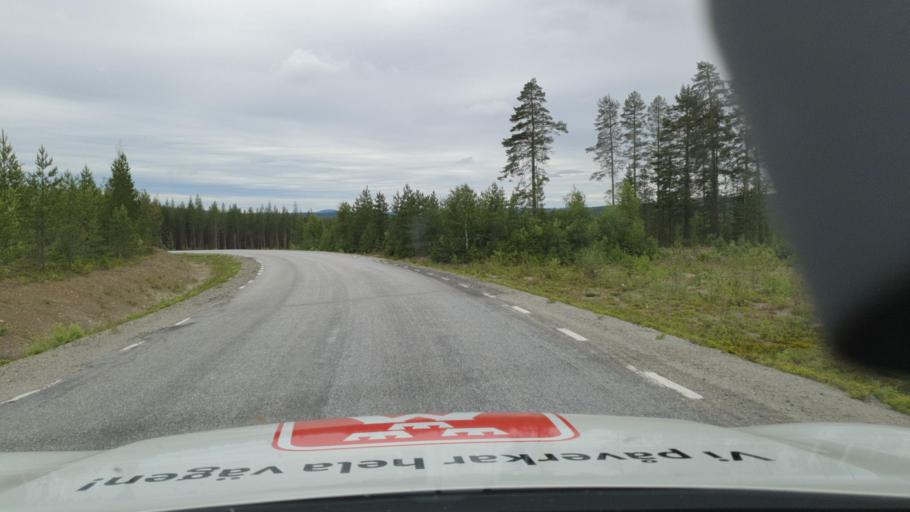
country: SE
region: Vaesterbotten
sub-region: Lycksele Kommun
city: Lycksele
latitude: 64.1291
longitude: 18.3597
